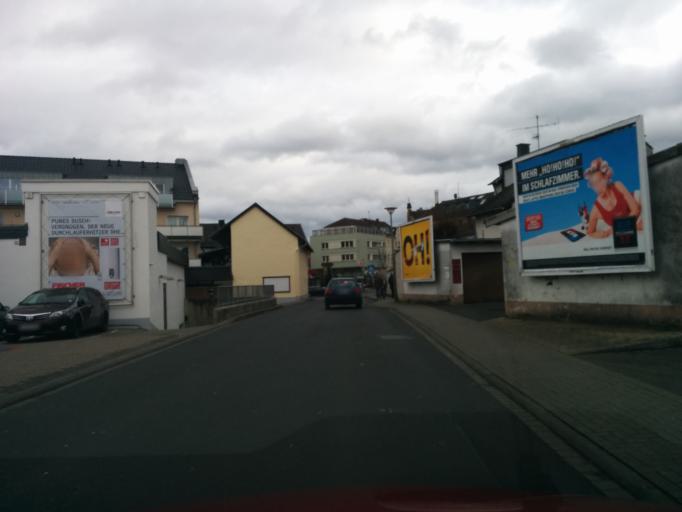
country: DE
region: North Rhine-Westphalia
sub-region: Regierungsbezirk Koln
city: Rheinbach
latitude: 50.6276
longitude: 6.9440
